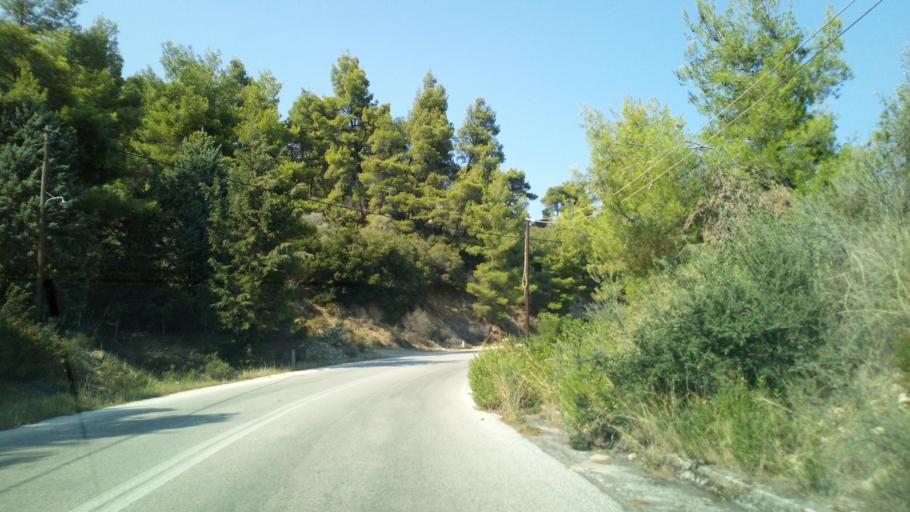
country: GR
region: Central Macedonia
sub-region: Nomos Chalkidikis
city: Sarti
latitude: 40.1109
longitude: 23.9846
